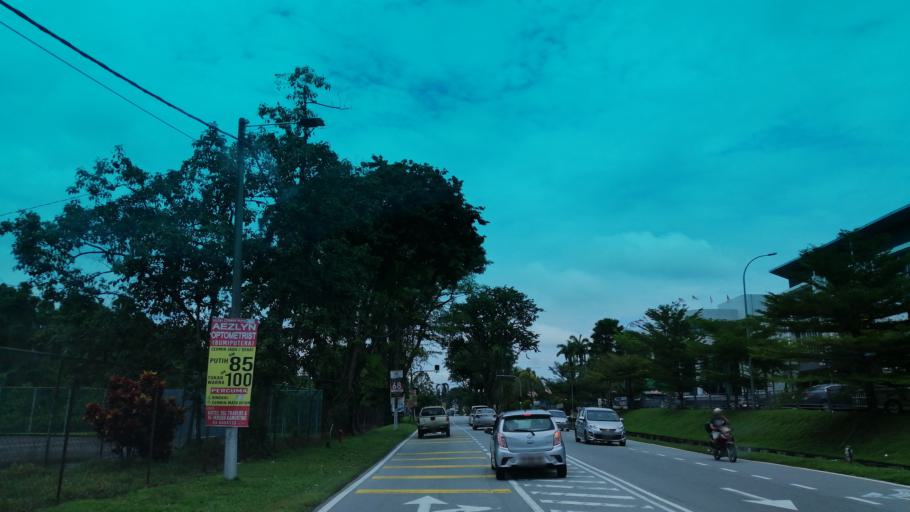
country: MY
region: Perak
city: Taiping
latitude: 4.8608
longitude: 100.7367
